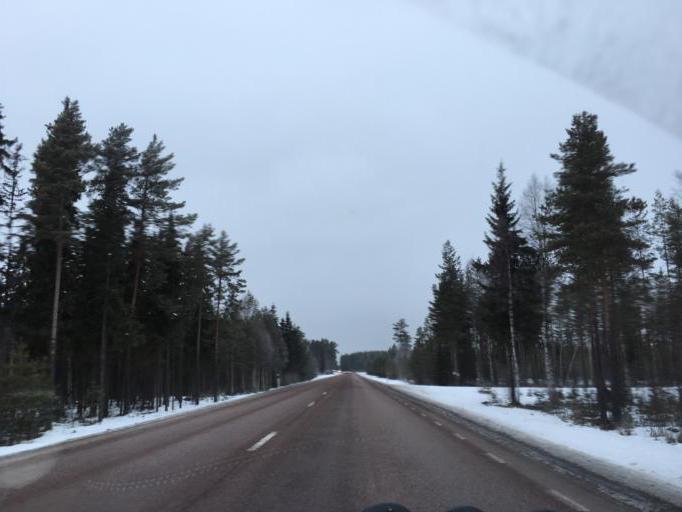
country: SE
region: Dalarna
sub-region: Mora Kommun
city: Mora
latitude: 60.9747
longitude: 14.6962
